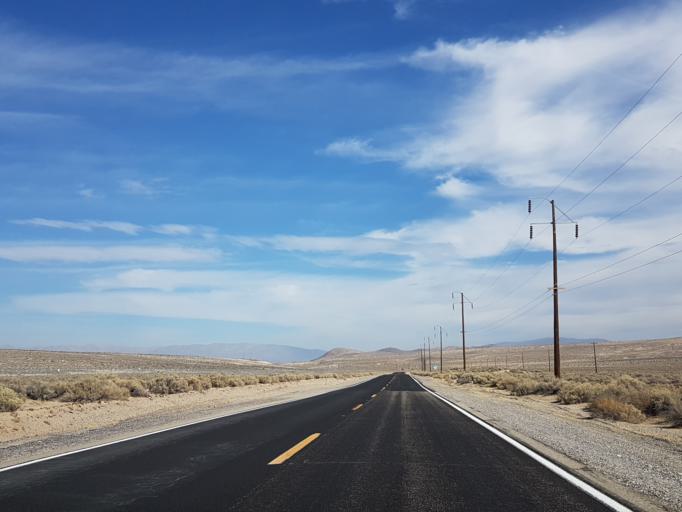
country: US
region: California
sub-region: San Bernardino County
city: Searles Valley
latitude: 35.6487
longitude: -117.4876
